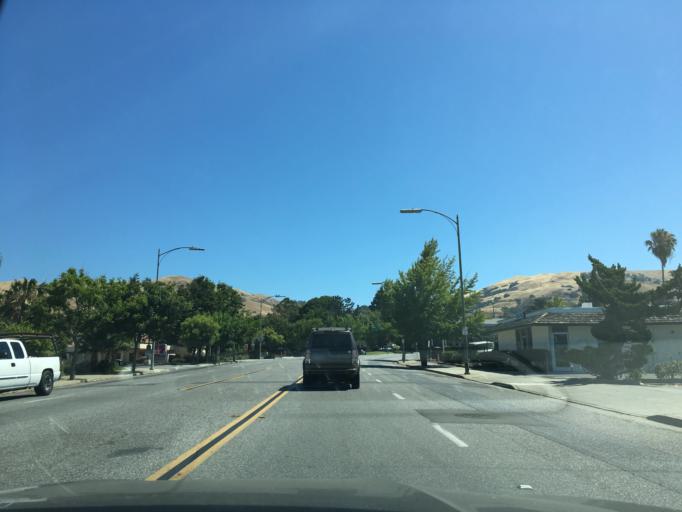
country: US
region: California
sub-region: Santa Clara County
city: East Foothills
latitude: 37.3803
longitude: -121.8278
